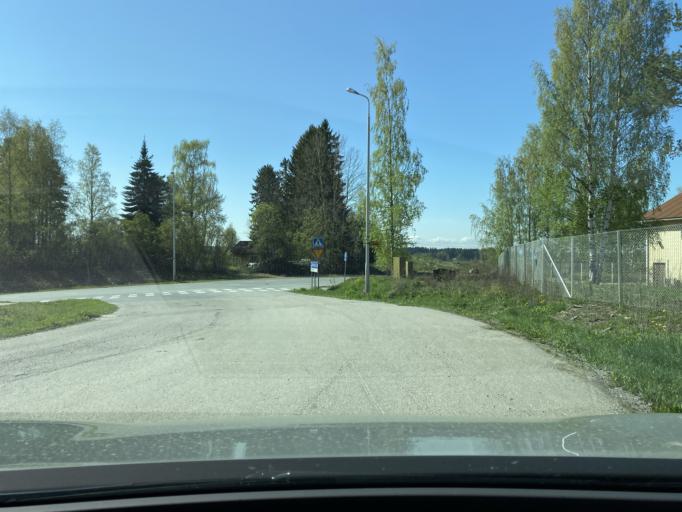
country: FI
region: Pirkanmaa
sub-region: Lounais-Pirkanmaa
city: Vammala
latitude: 61.3505
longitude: 22.8809
